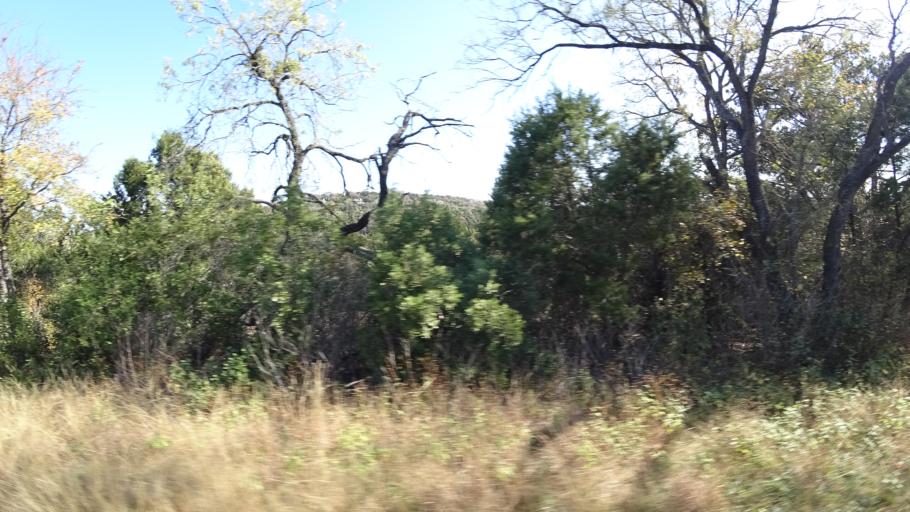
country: US
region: Texas
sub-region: Williamson County
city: Jollyville
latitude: 30.3880
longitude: -97.7737
